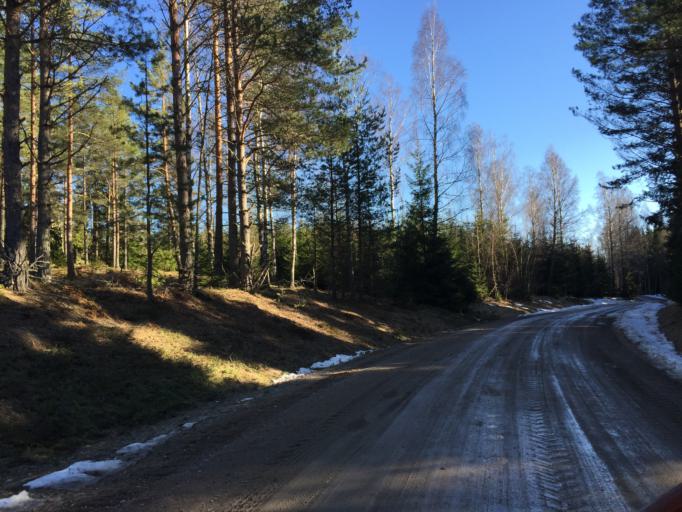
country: SE
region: OErebro
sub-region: Orebro Kommun
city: Odensbacken
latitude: 58.9969
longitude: 15.6173
